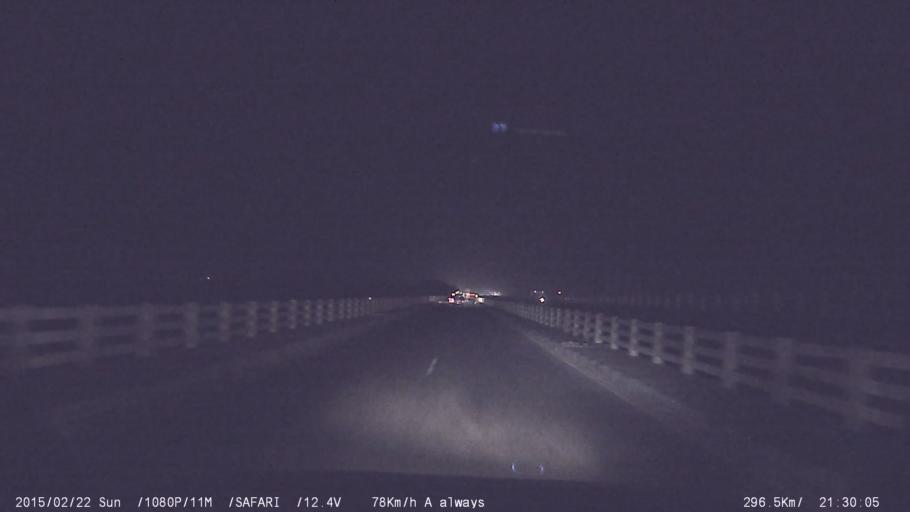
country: IN
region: Tamil Nadu
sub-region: Karur
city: Karur
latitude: 10.9412
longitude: 78.0569
